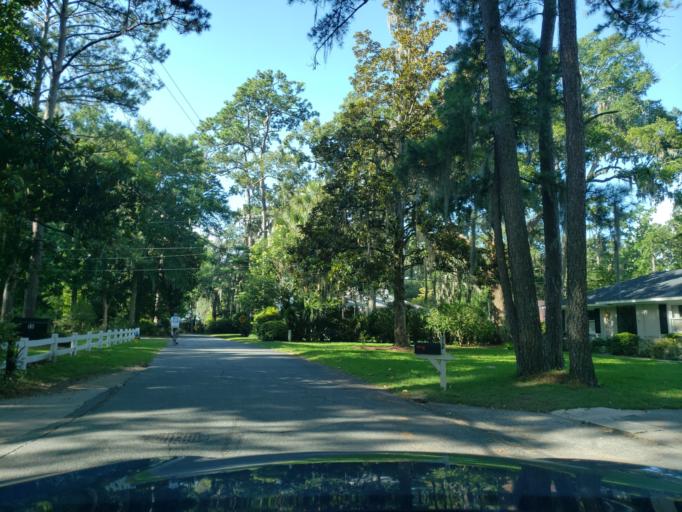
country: US
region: Georgia
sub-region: Chatham County
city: Isle of Hope
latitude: 31.9750
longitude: -81.0578
